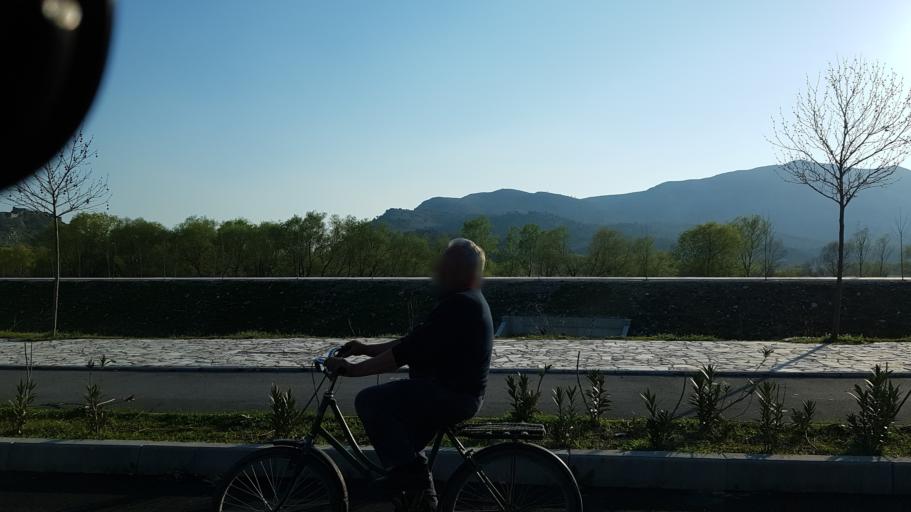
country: AL
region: Shkoder
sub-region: Rrethi i Shkodres
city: Shkoder
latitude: 42.0601
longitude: 19.4967
